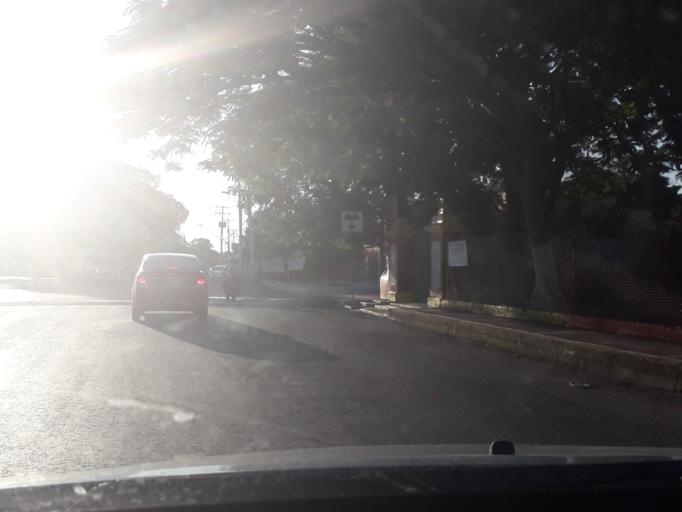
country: MX
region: Yucatan
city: Merida
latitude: 20.9664
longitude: -89.6442
